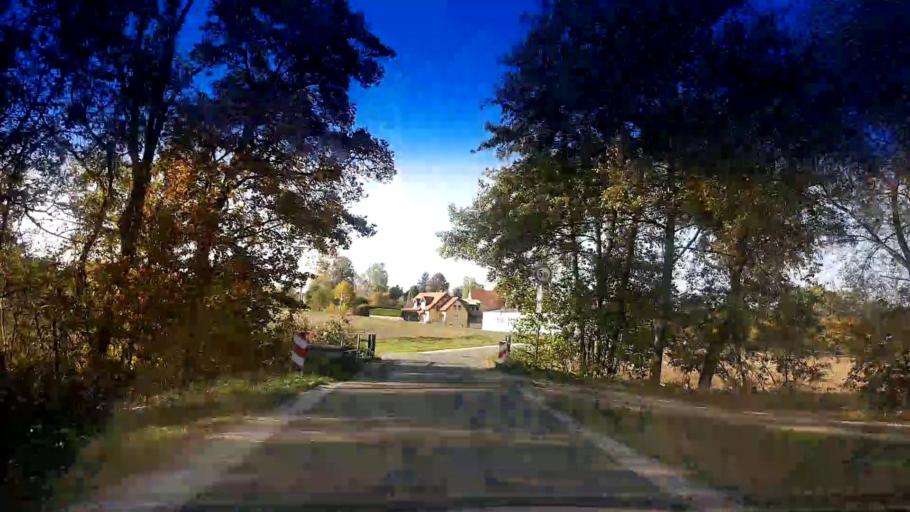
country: DE
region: Bavaria
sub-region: Upper Franconia
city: Strullendorf
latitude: 49.8631
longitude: 10.9975
